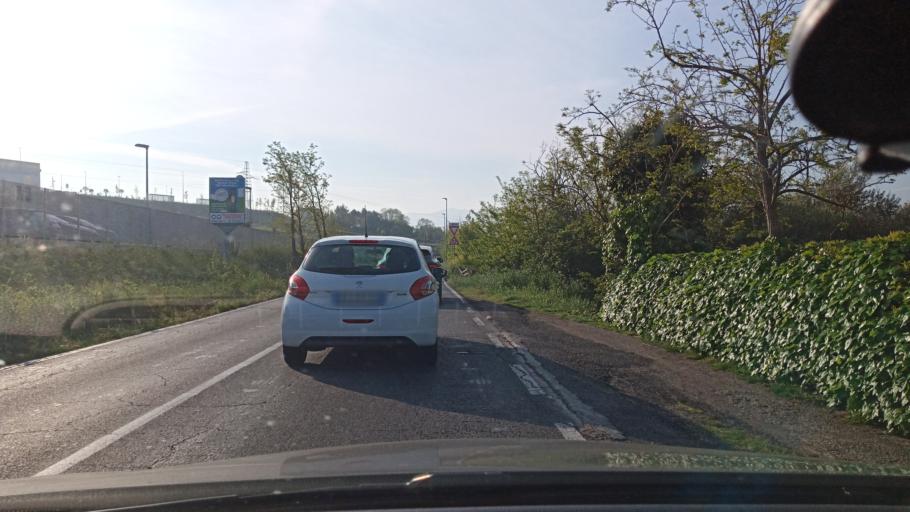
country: IT
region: Latium
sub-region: Citta metropolitana di Roma Capitale
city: Fiano Romano
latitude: 42.1673
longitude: 12.6401
